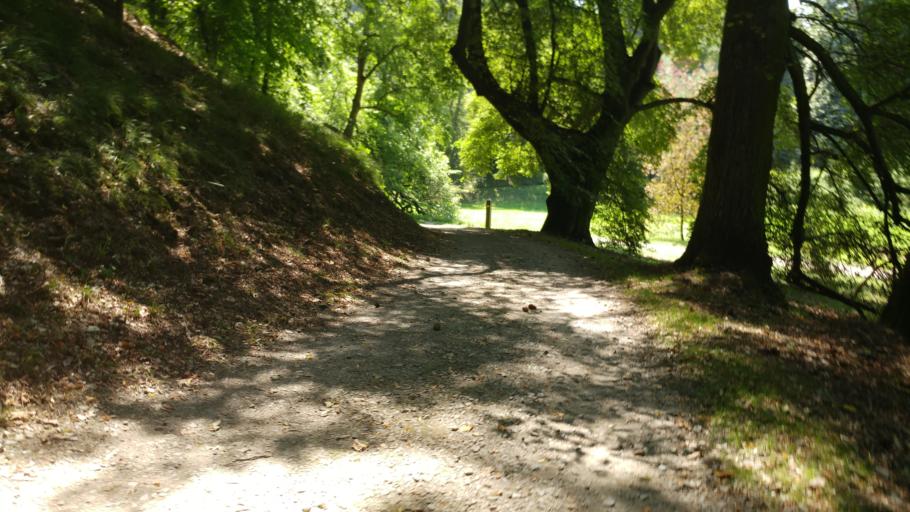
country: CZ
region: Central Bohemia
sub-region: Okres Praha-Zapad
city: Pruhonice
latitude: 49.9914
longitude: 14.5606
